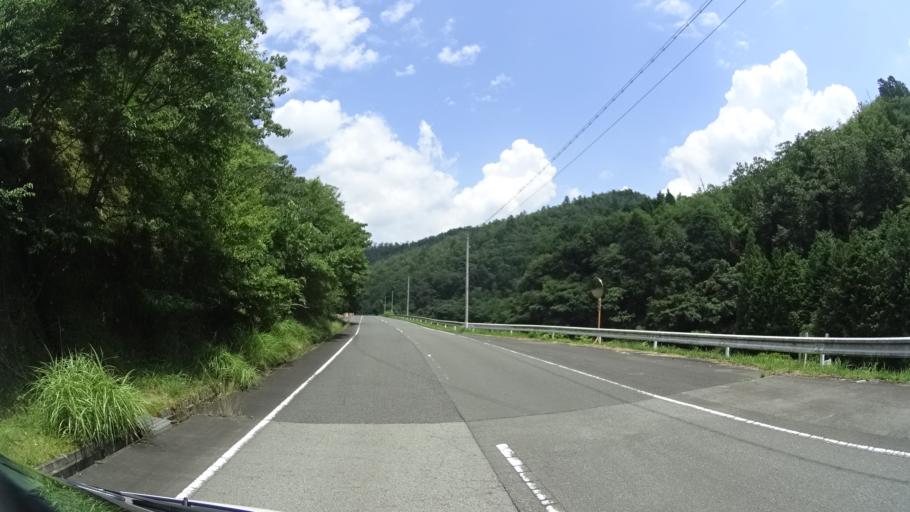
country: JP
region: Hyogo
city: Sasayama
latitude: 35.1796
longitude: 135.2441
